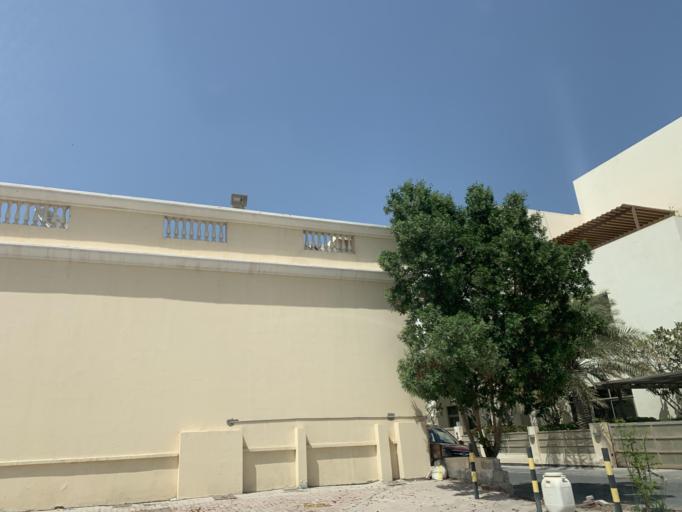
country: BH
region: Northern
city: Madinat `Isa
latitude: 26.1551
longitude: 50.5502
